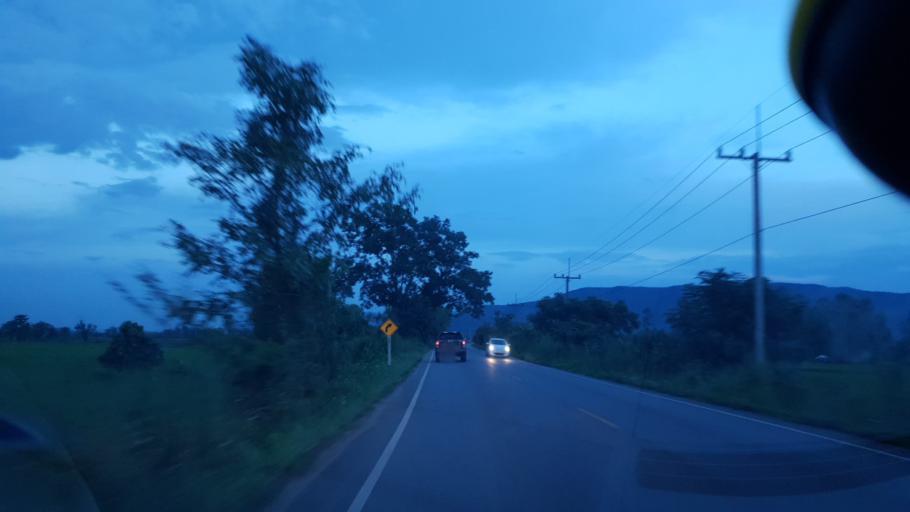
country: TH
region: Chiang Rai
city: Wiang Chiang Rung
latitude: 19.9653
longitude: 99.9896
